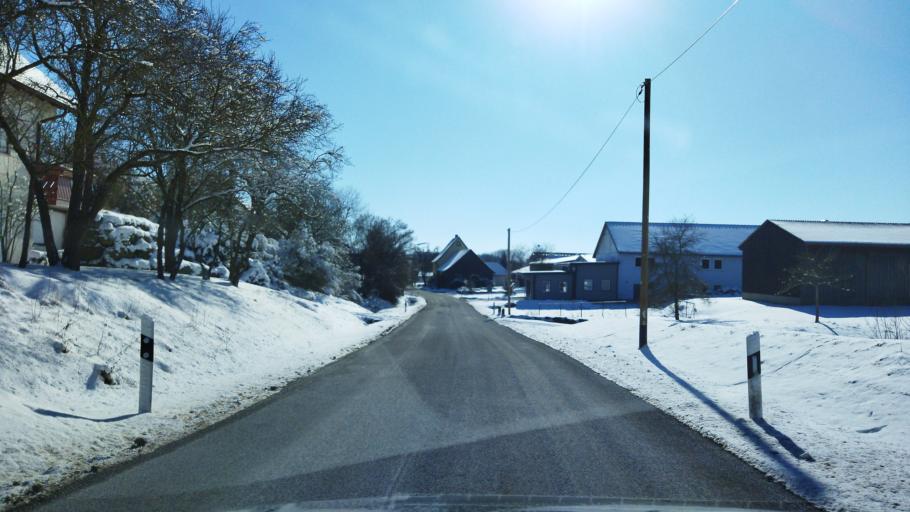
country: DE
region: Baden-Wuerttemberg
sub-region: Regierungsbezirk Stuttgart
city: Langenburg
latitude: 49.2512
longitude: 9.8920
